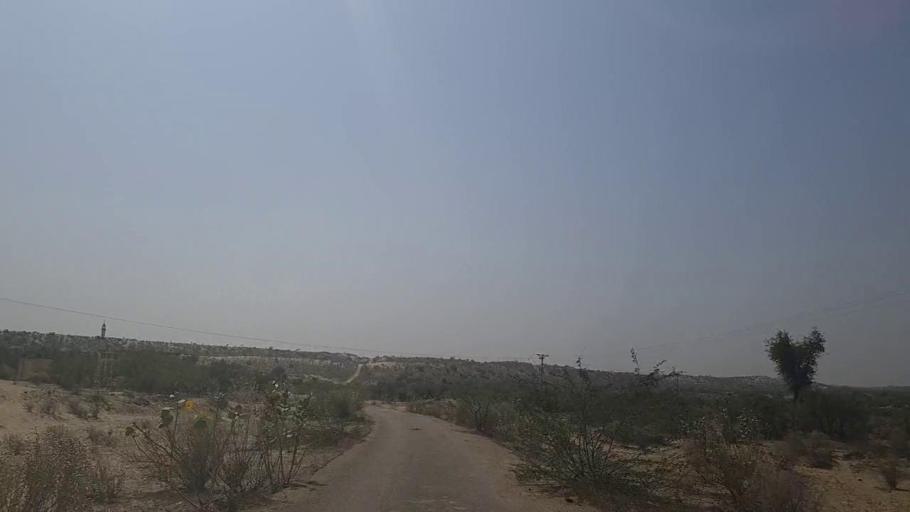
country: PK
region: Sindh
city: Naukot
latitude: 24.8229
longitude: 69.4813
